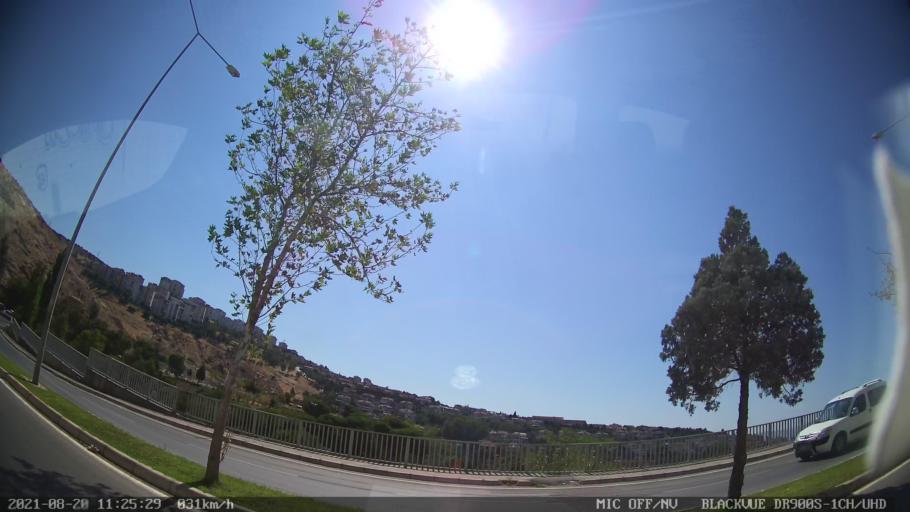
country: TR
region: Izmir
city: Karsiyaka
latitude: 38.5047
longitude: 27.0809
